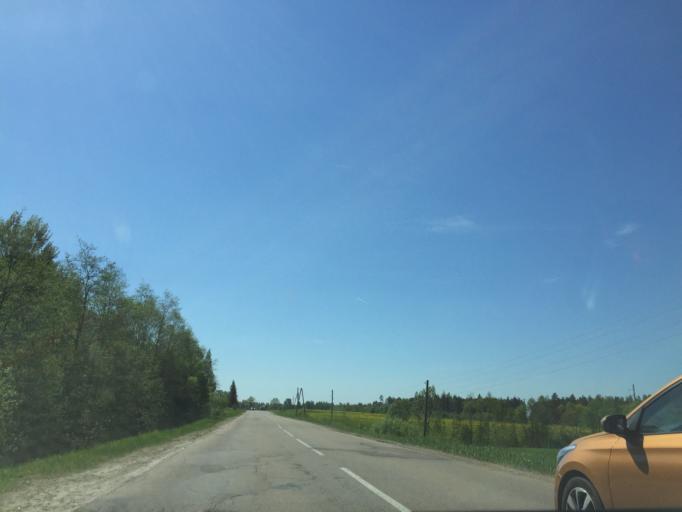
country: LV
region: Malpils
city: Malpils
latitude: 56.9247
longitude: 24.9375
